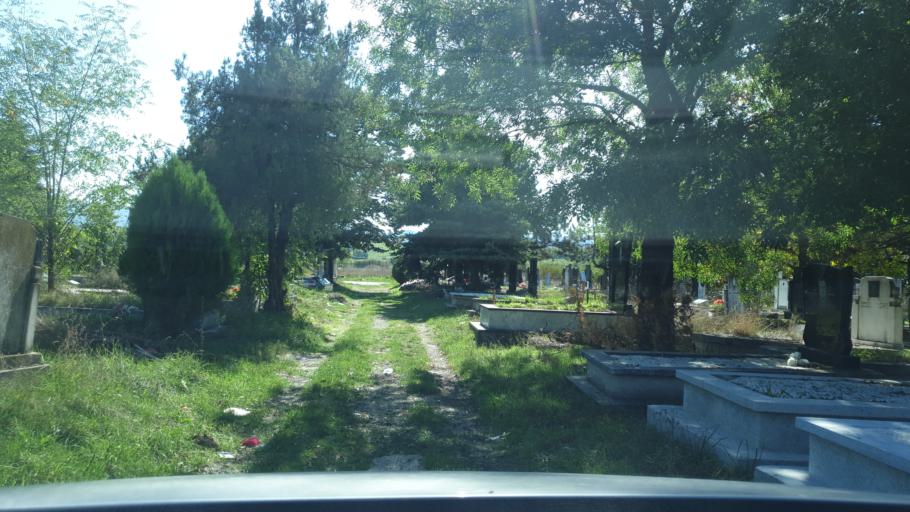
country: XK
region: Gjakova
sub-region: Komuna e Gjakoves
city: Gjakove
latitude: 42.3706
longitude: 20.4078
